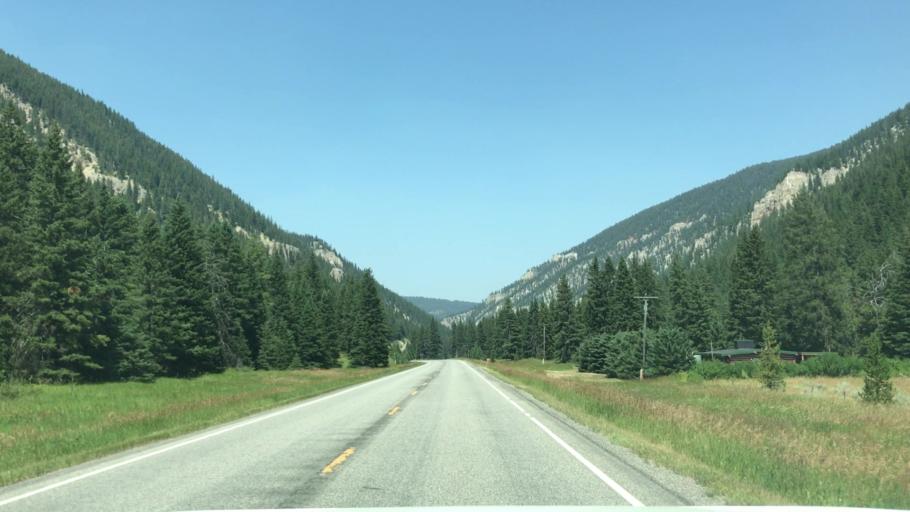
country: US
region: Montana
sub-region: Gallatin County
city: Big Sky
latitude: 45.1233
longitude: -111.2296
